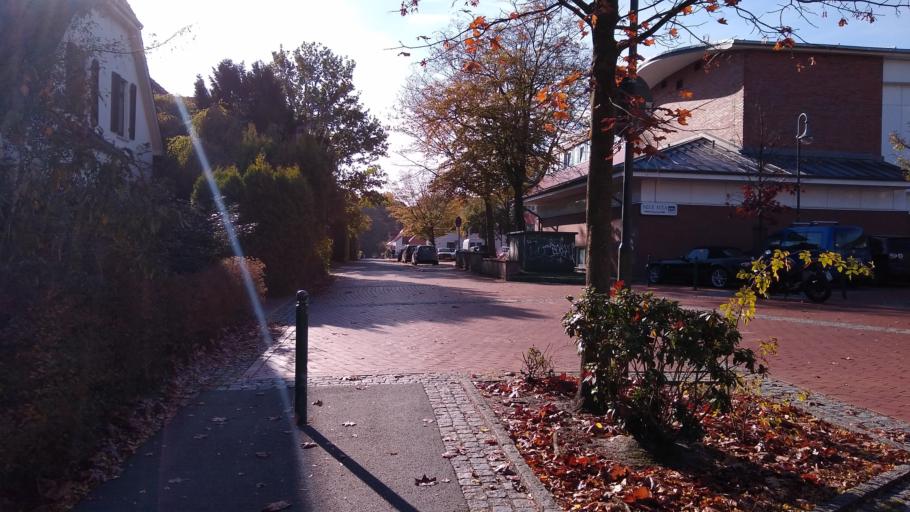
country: DE
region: Lower Saxony
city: Rastede
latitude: 53.2448
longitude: 8.1974
